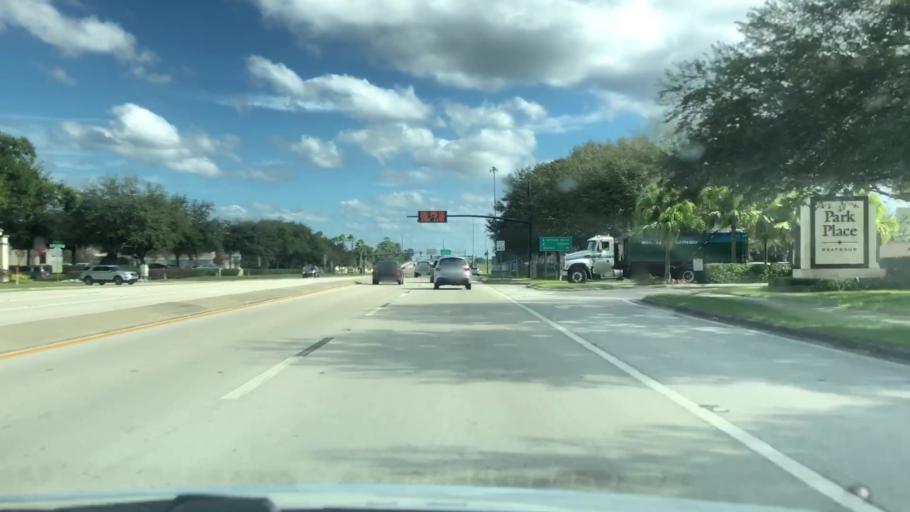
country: US
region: Florida
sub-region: Seminole County
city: Heathrow
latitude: 28.7864
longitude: -81.3570
